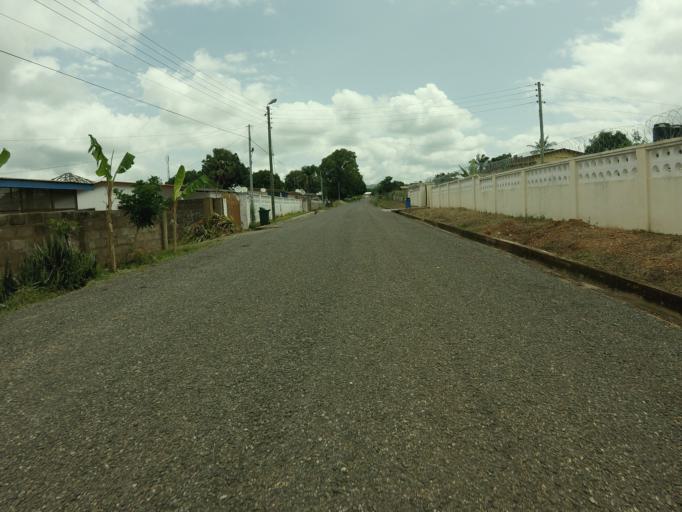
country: GH
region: Volta
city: Ho
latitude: 6.5902
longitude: 0.4775
